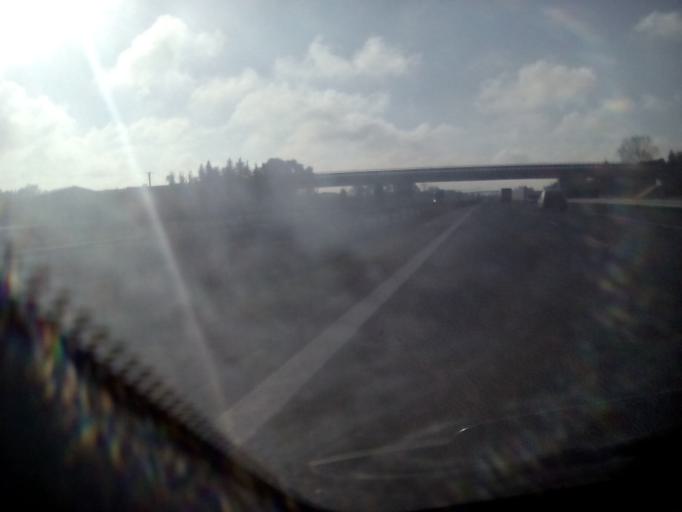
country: PL
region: Masovian Voivodeship
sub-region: Powiat grojecki
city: Jasieniec
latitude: 51.7996
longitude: 20.8894
